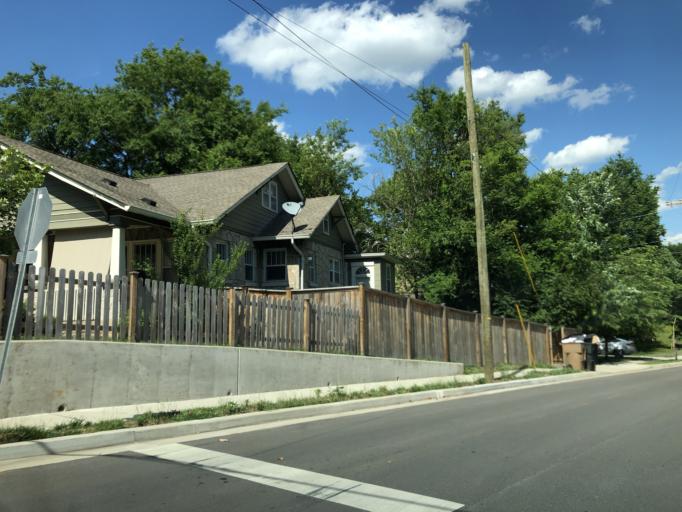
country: US
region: Tennessee
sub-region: Davidson County
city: Nashville
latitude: 36.1843
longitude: -86.7377
